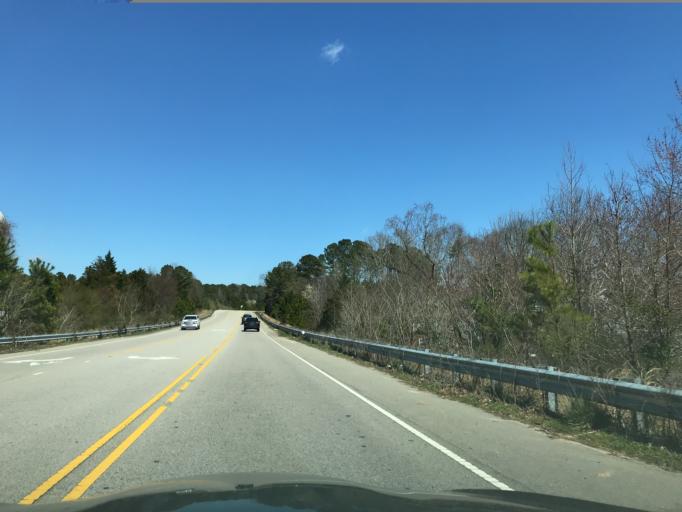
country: US
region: North Carolina
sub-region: Wake County
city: Wake Forest
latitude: 35.9664
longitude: -78.5612
